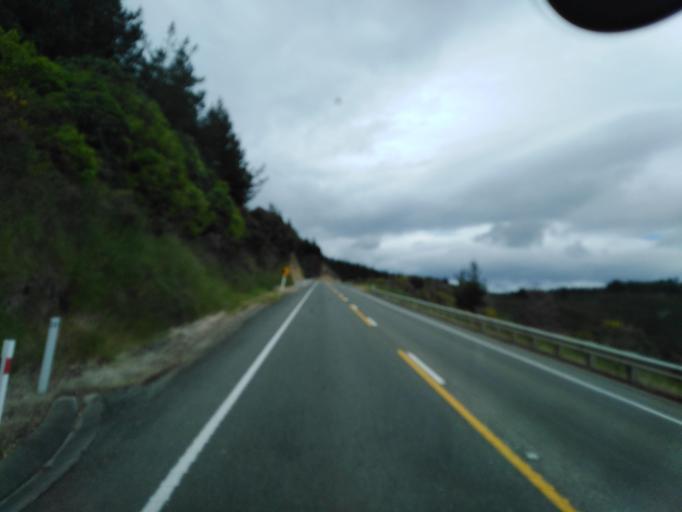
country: NZ
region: Tasman
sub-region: Tasman District
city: Wakefield
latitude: -41.4794
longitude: 172.9188
